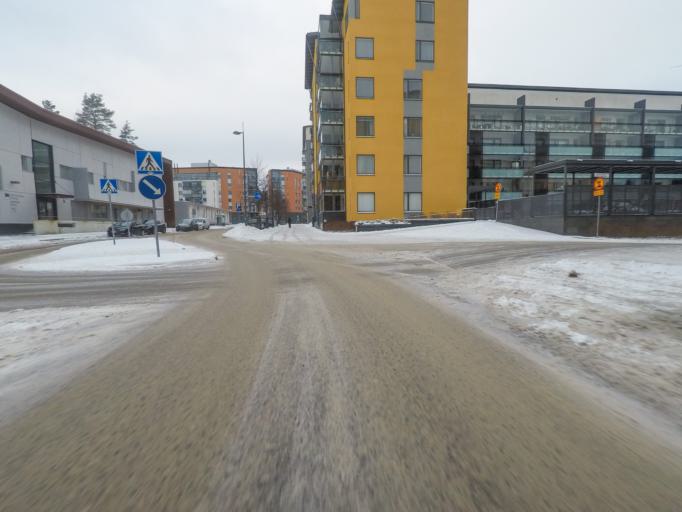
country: FI
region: Uusimaa
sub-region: Helsinki
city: Vantaa
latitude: 60.2043
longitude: 25.1587
